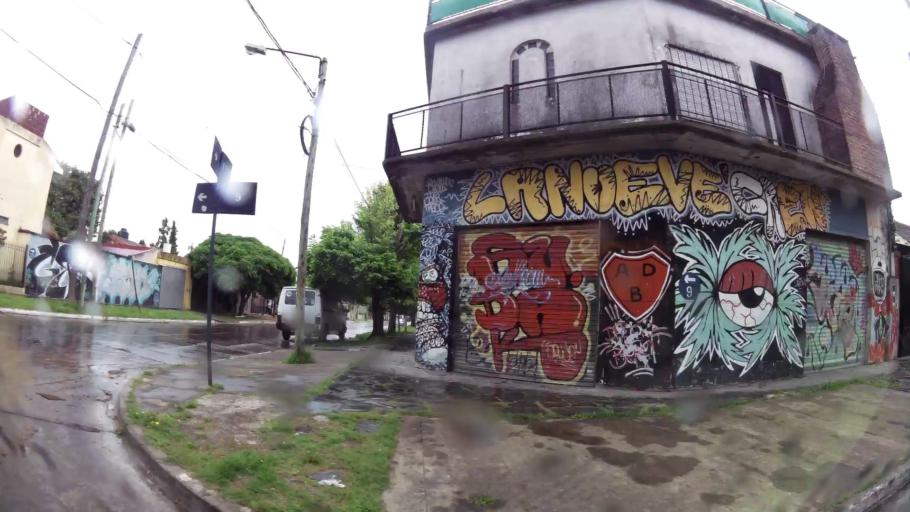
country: AR
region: Buenos Aires
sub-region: Partido de Quilmes
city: Quilmes
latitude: -34.7650
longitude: -58.2286
